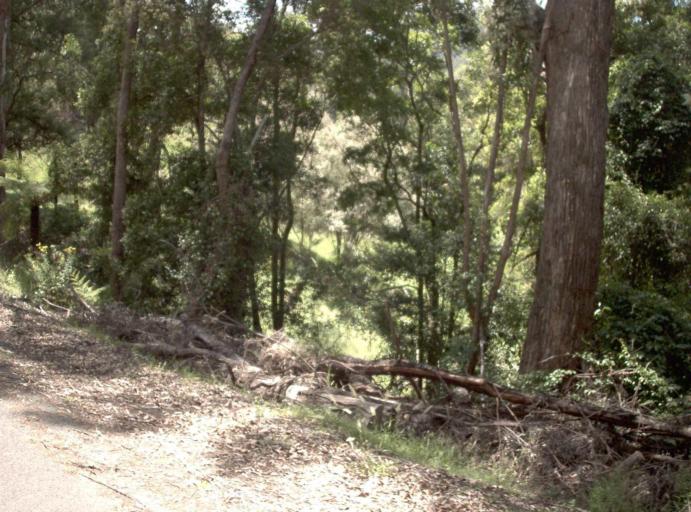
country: AU
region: New South Wales
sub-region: Bombala
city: Bombala
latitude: -37.5194
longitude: 148.9293
